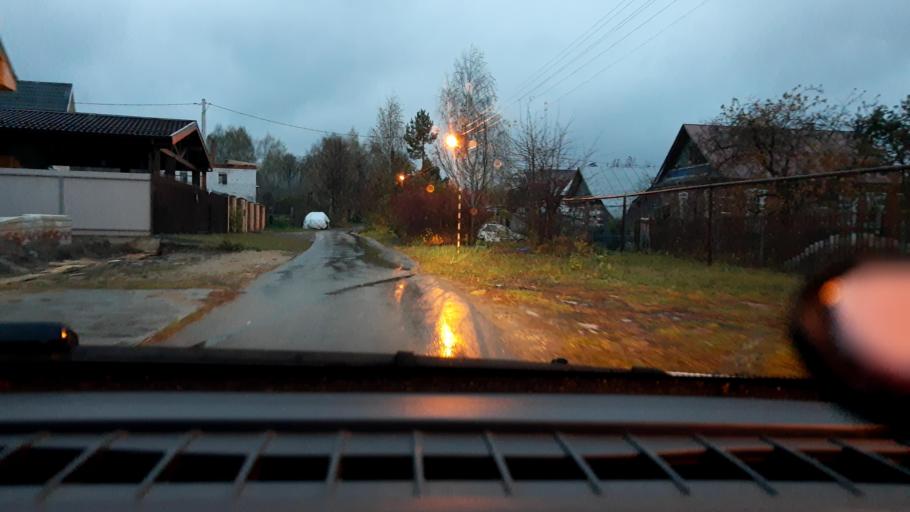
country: RU
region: Nizjnij Novgorod
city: Afonino
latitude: 56.2253
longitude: 44.1016
